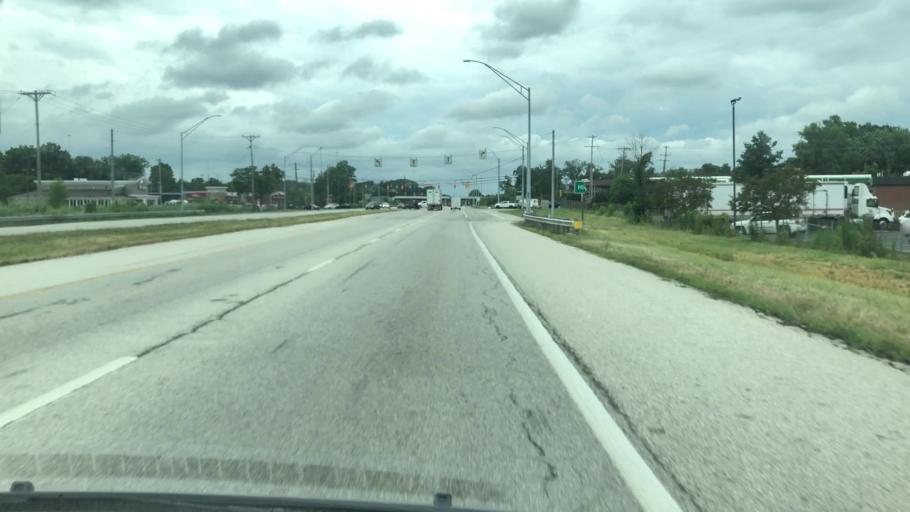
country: US
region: Ohio
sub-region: Summit County
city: Macedonia
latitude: 41.2975
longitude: -81.5139
